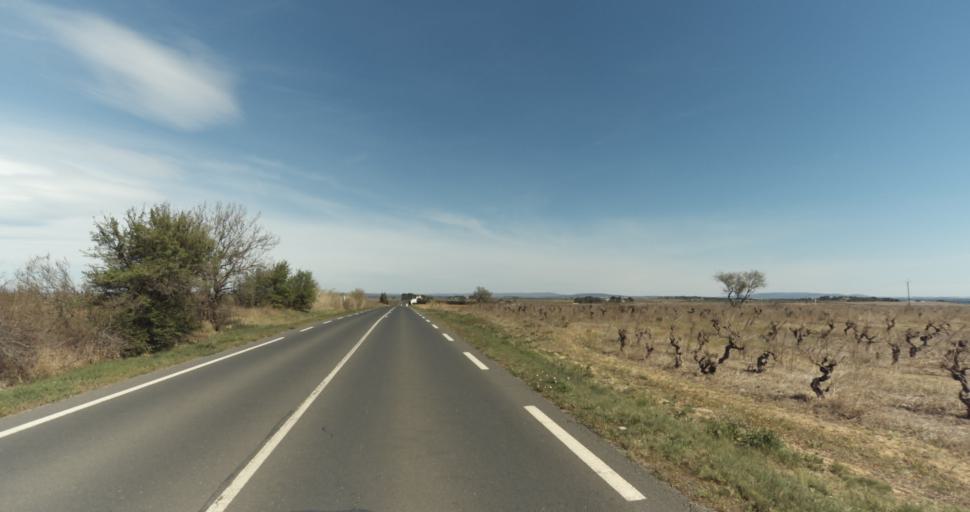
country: FR
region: Languedoc-Roussillon
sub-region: Departement de l'Herault
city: Marseillan
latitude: 43.3746
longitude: 3.5338
